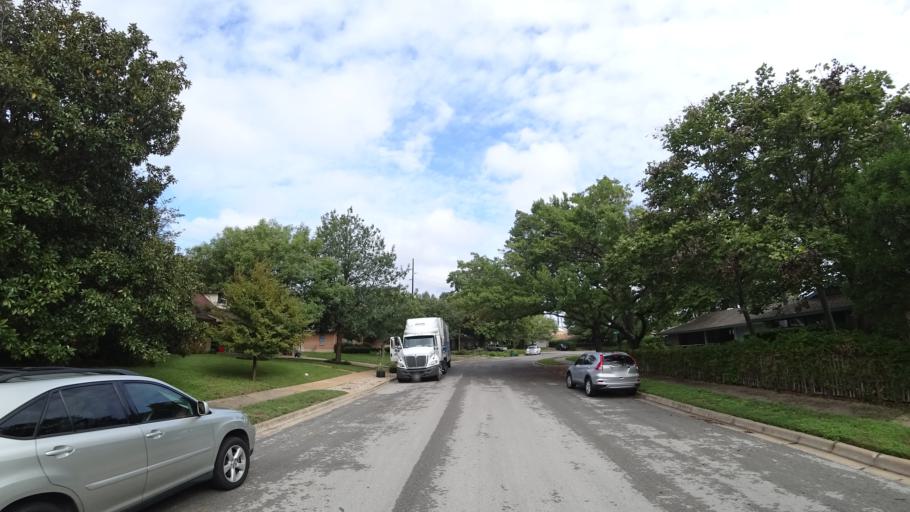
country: US
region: Texas
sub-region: Travis County
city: West Lake Hills
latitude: 30.3417
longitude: -97.7512
